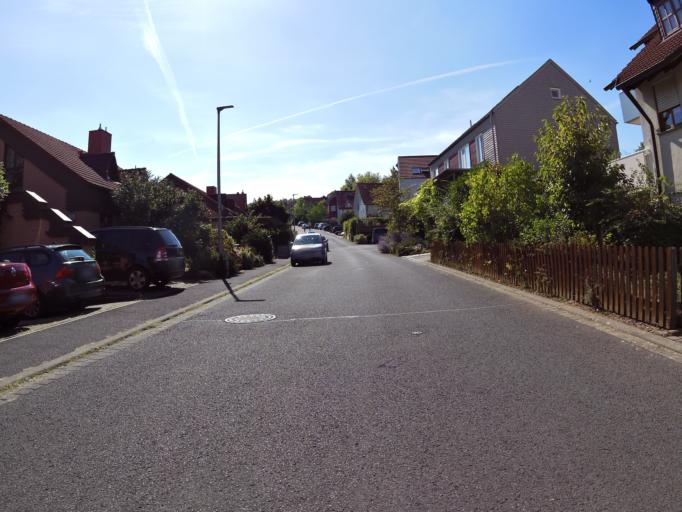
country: DE
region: Bavaria
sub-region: Regierungsbezirk Unterfranken
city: Margetshochheim
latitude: 49.8420
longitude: 9.8573
